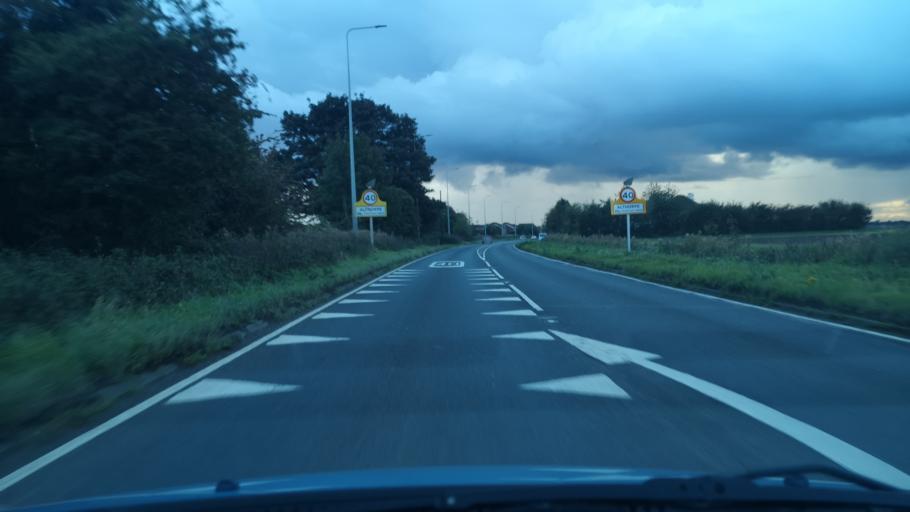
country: GB
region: England
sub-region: North Lincolnshire
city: Gunness
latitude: 53.5806
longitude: -0.7398
